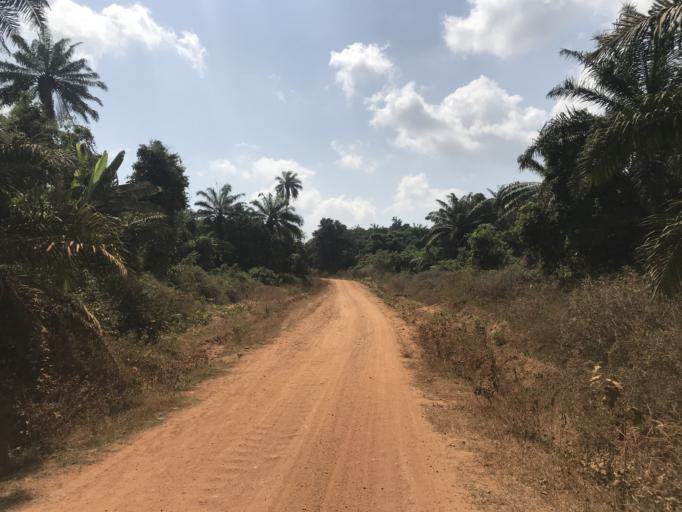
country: NG
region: Osun
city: Ifon
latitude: 7.9632
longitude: 4.4993
